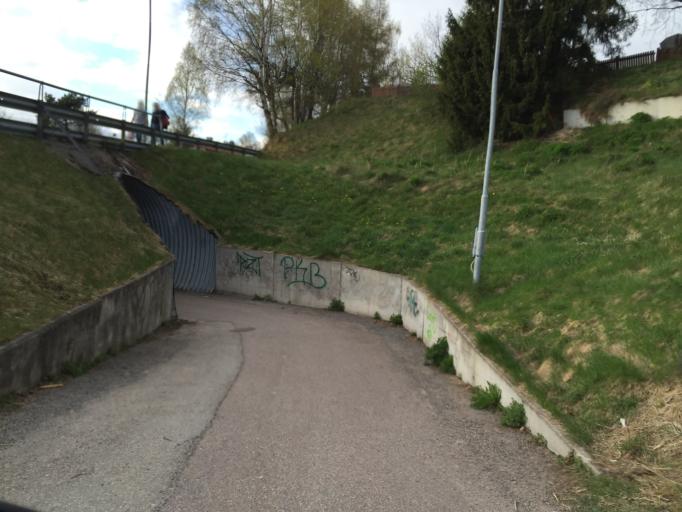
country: SE
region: Dalarna
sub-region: Ludvika Kommun
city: Ludvika
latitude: 60.1339
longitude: 15.1766
